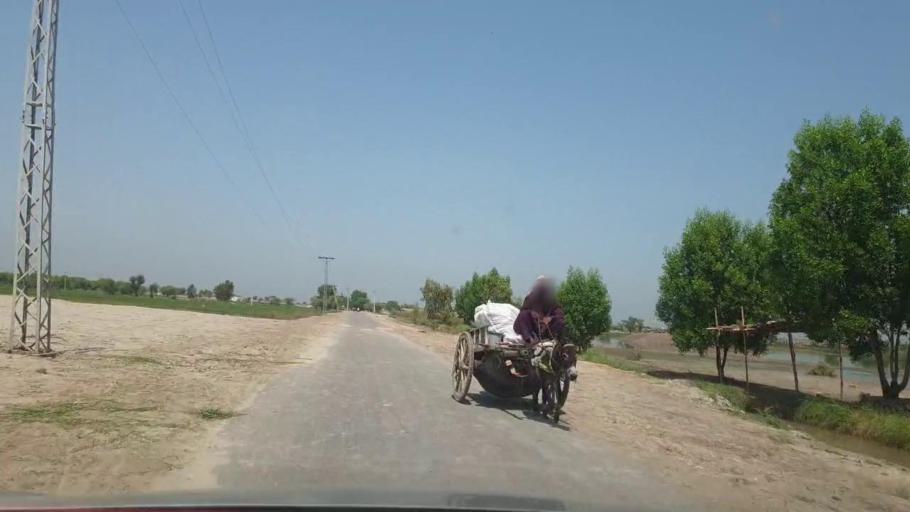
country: PK
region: Sindh
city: Warah
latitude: 27.4770
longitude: 67.7575
